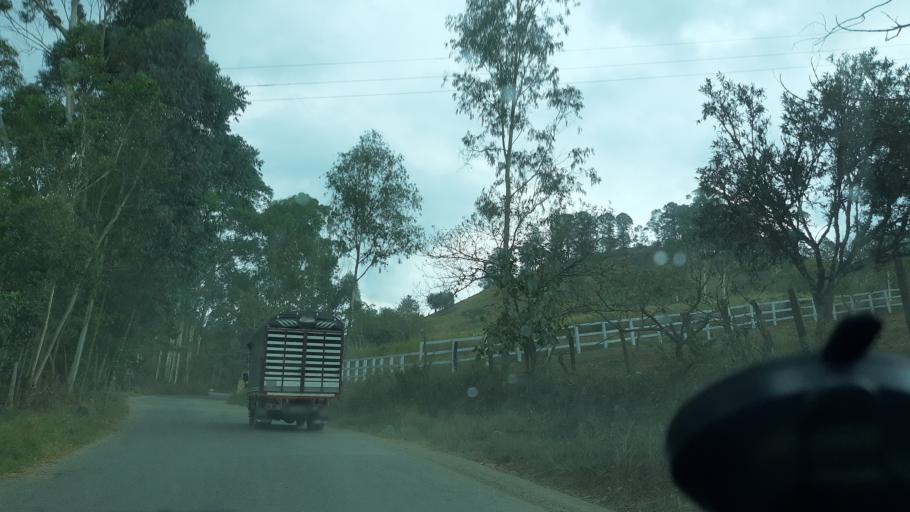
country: CO
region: Boyaca
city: Garagoa
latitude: 5.0756
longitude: -73.3736
